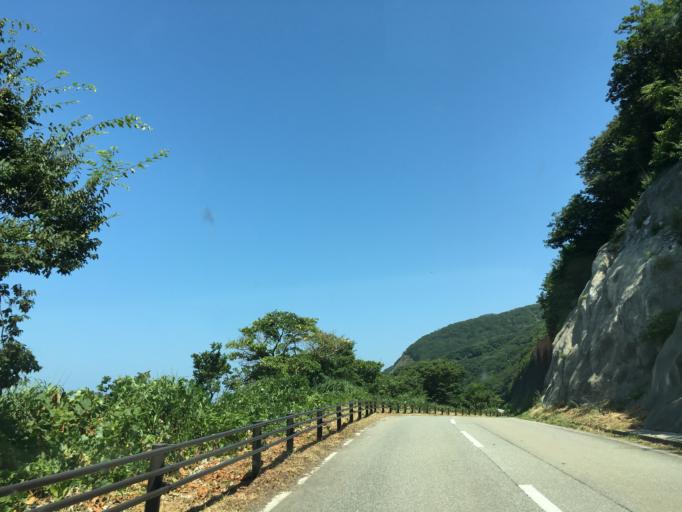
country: JP
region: Akita
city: Tenno
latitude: 39.8782
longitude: 139.7429
